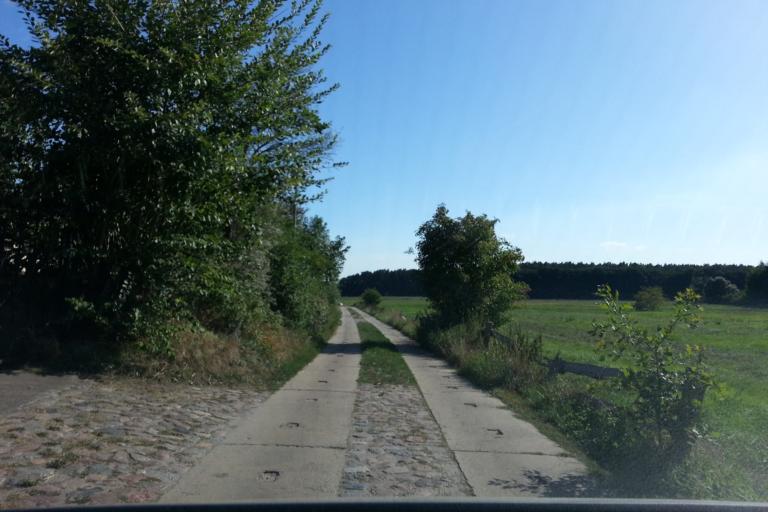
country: DE
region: Mecklenburg-Vorpommern
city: Torgelow
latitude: 53.6253
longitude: 14.0042
